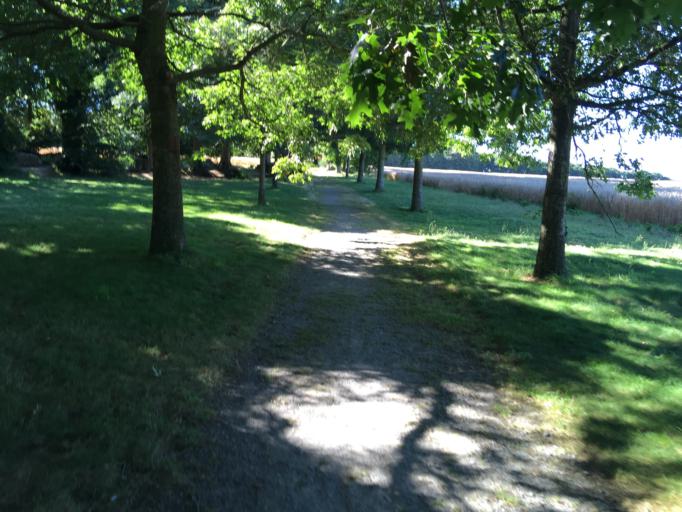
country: FR
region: Brittany
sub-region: Departement des Cotes-d'Armor
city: Pleslin-Trigavou
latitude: 48.5296
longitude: -2.0587
